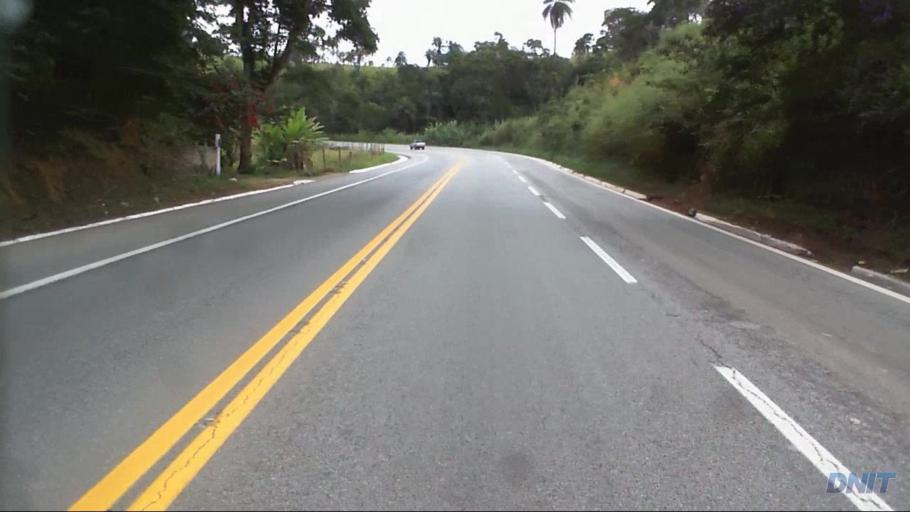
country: BR
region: Minas Gerais
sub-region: Caete
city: Caete
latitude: -19.7505
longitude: -43.6271
